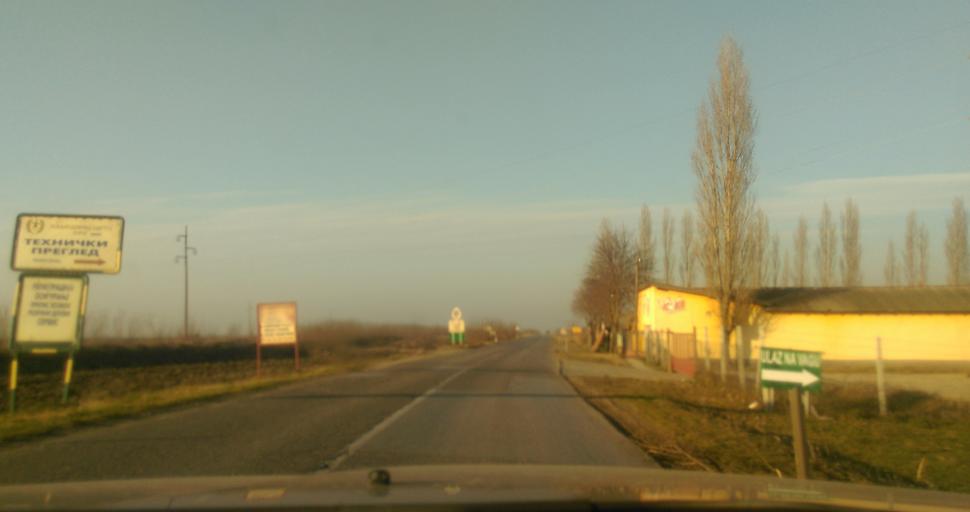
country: RS
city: Curug
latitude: 45.4745
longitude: 20.0440
